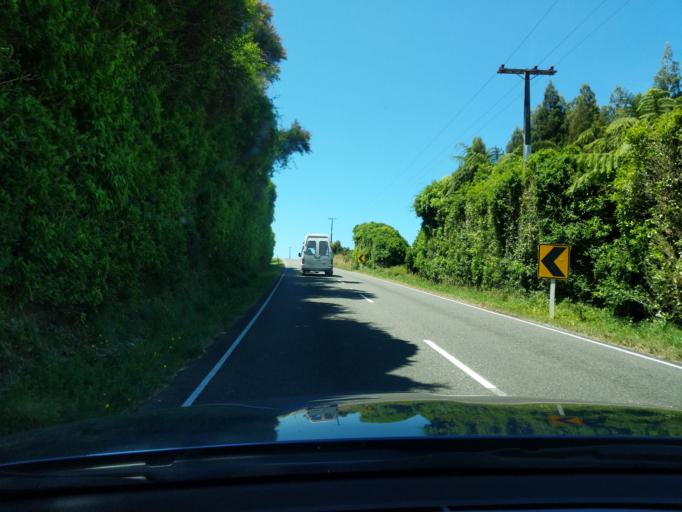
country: NZ
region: Tasman
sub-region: Tasman District
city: Takaka
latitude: -40.6937
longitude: 172.6398
